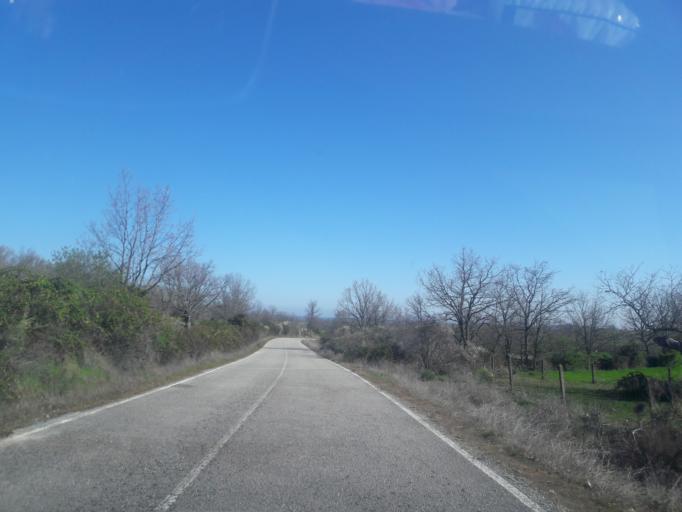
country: ES
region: Castille and Leon
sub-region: Provincia de Salamanca
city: Cabeza del Caballo
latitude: 41.1438
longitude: -6.5573
